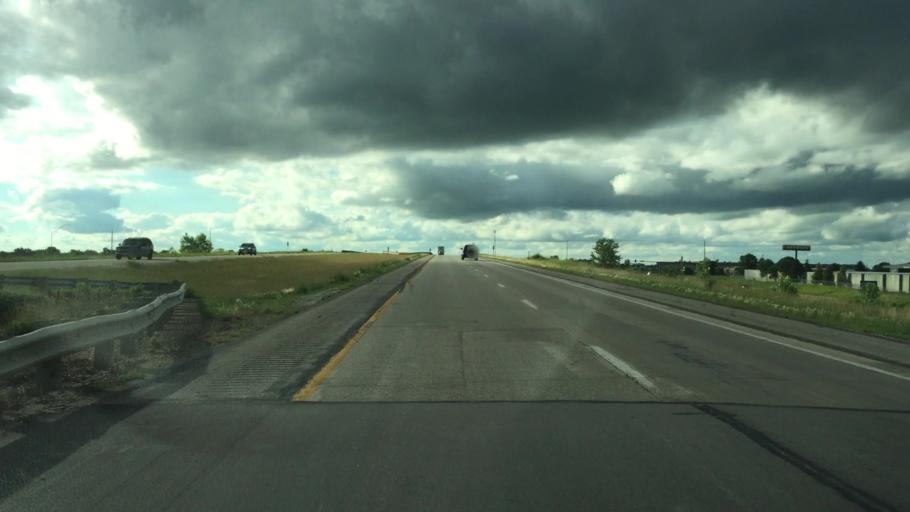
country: US
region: Iowa
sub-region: Polk County
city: Altoona
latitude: 41.6448
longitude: -93.5107
